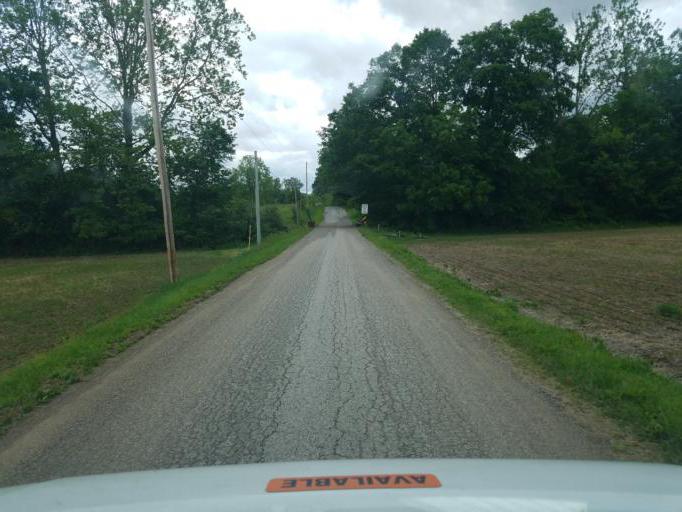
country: US
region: Ohio
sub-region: Richland County
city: Lexington
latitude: 40.6378
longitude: -82.6657
